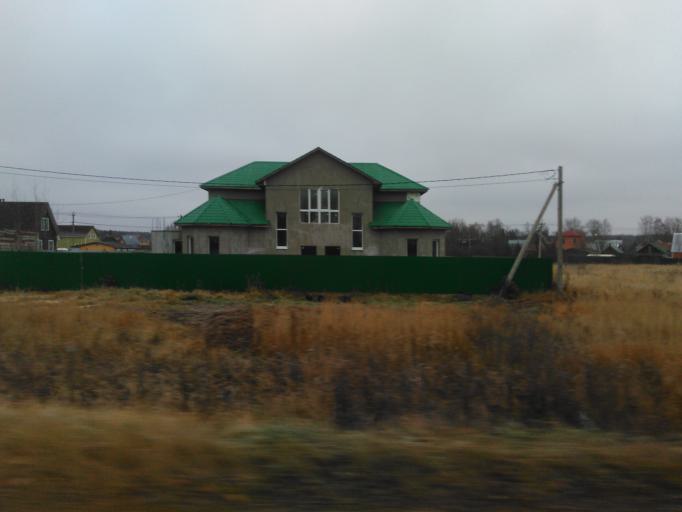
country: RU
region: Moskovskaya
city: Ashukino
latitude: 56.1729
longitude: 37.9395
